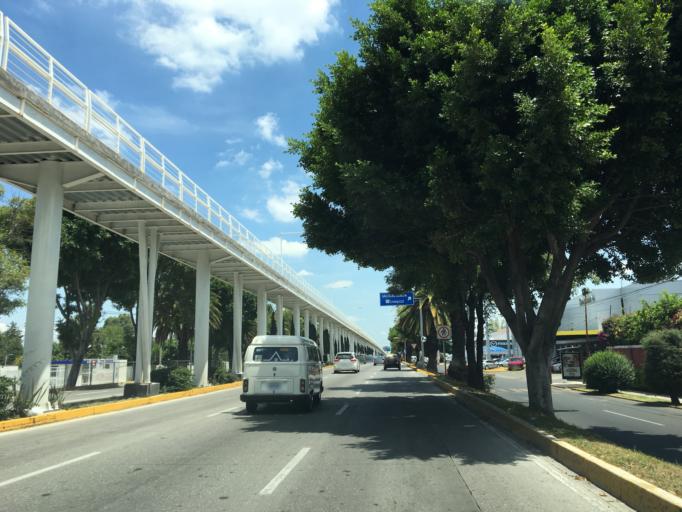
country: MX
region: Puebla
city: Puebla
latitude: 19.0653
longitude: -98.2229
